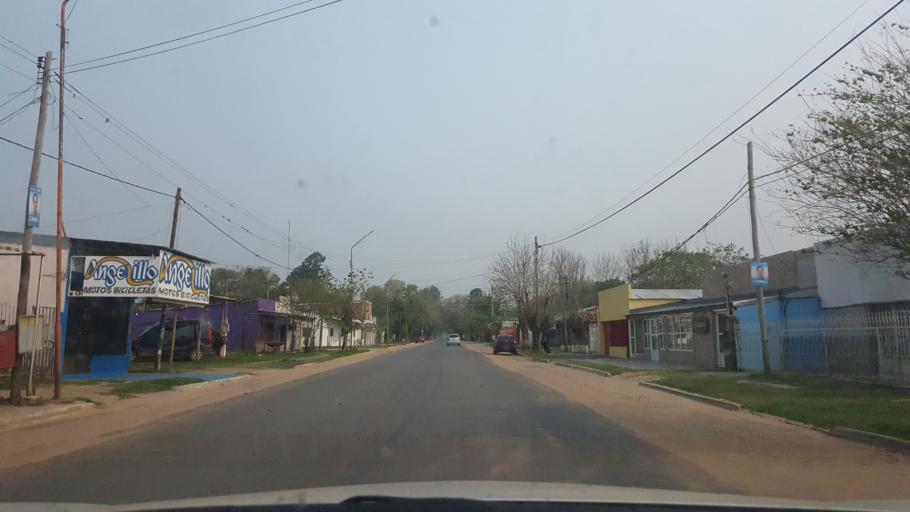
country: AR
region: Corrientes
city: Ita Ibate
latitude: -27.4277
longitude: -57.3380
